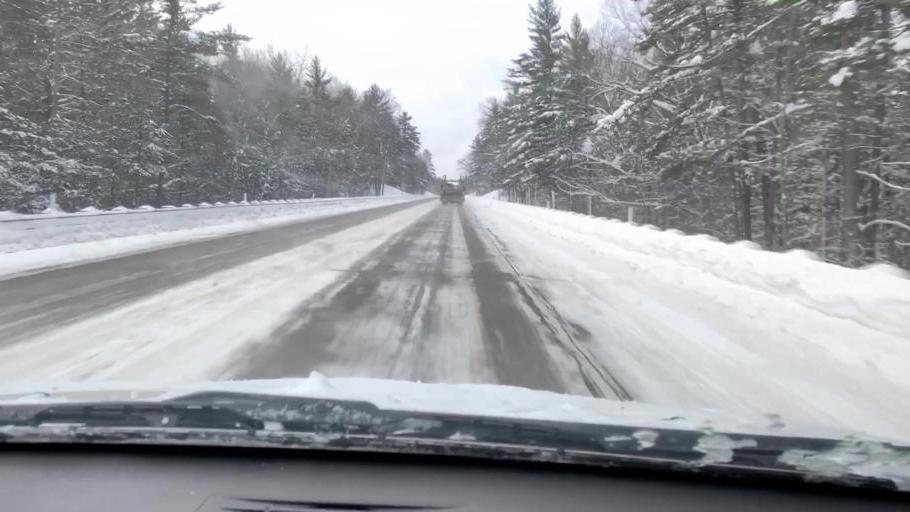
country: US
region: Michigan
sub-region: Wexford County
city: Manton
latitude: 44.5734
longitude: -85.3648
